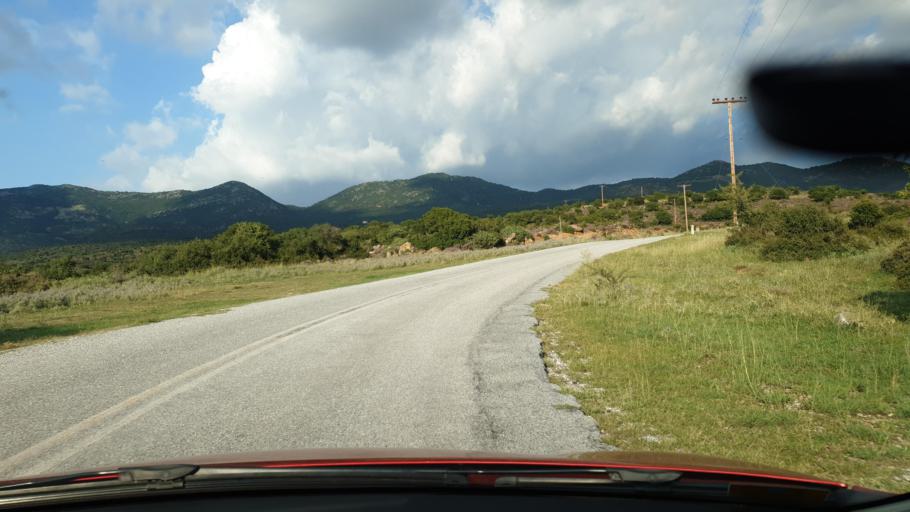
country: GR
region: Central Macedonia
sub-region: Nomos Thessalonikis
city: Peristera
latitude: 40.5140
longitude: 23.1691
